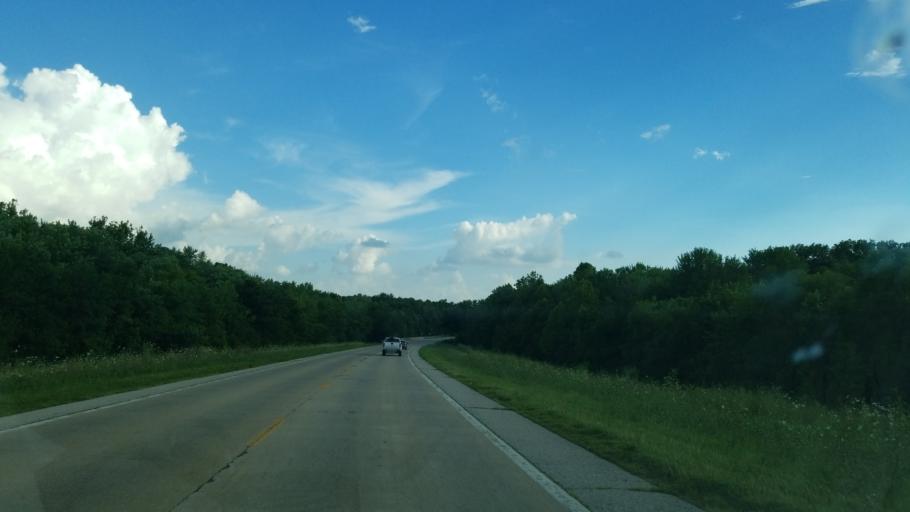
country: US
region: Illinois
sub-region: Marion County
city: Central City
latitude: 38.5760
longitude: -89.1087
